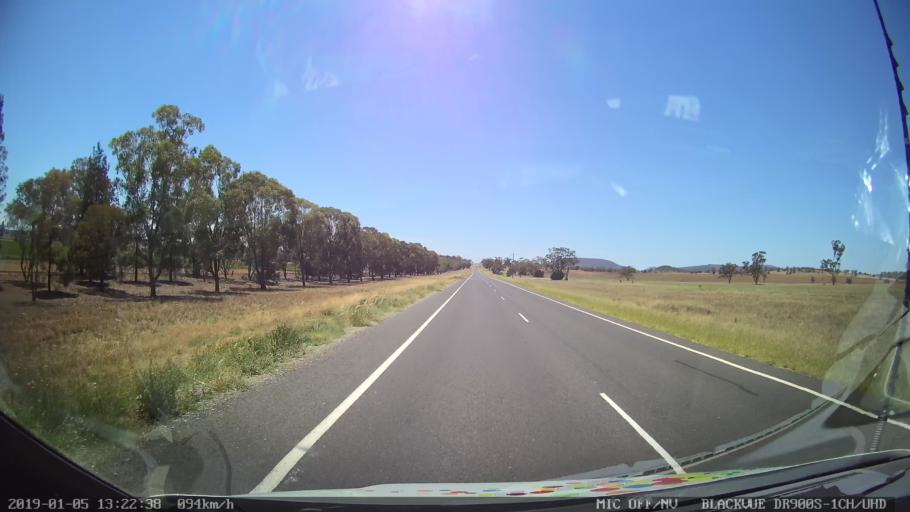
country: AU
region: New South Wales
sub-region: Gunnedah
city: Gunnedah
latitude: -31.0846
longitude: 149.9644
